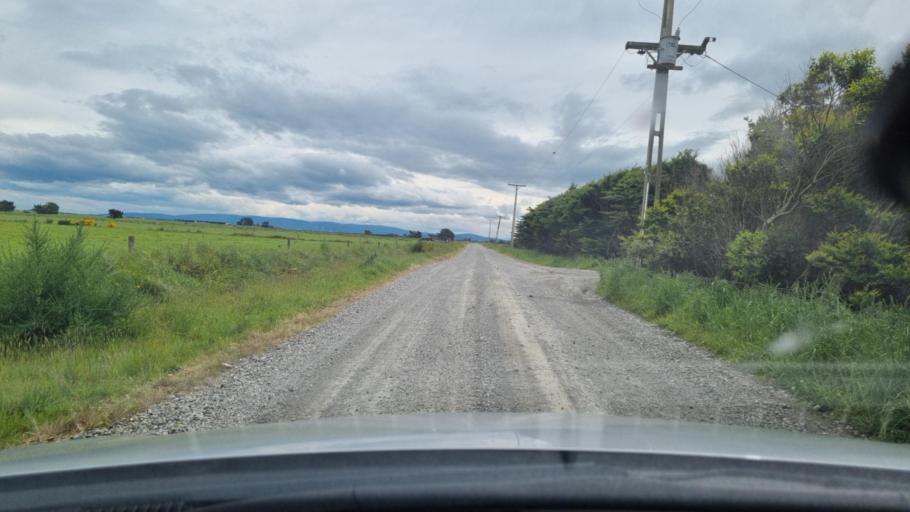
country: NZ
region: Southland
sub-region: Invercargill City
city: Invercargill
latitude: -46.4041
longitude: 168.2879
